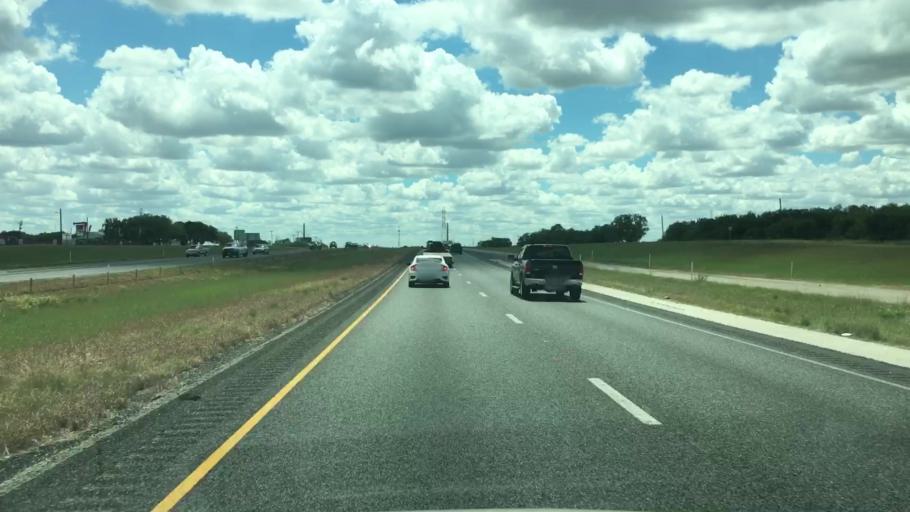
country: US
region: Texas
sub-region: Bexar County
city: Elmendorf
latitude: 29.2777
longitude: -98.3961
